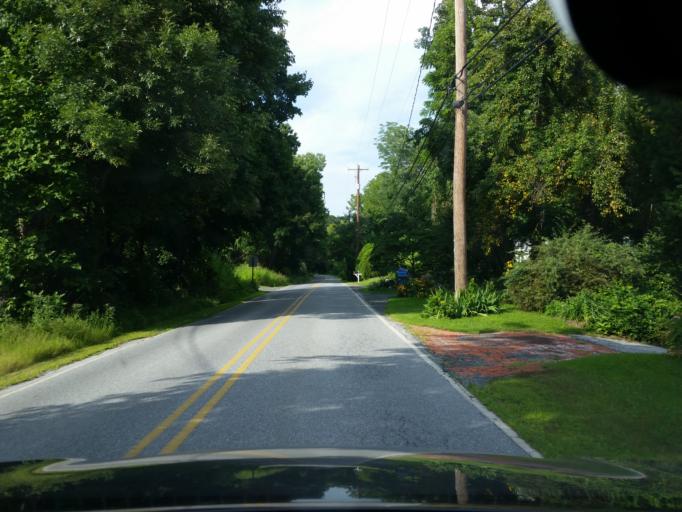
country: US
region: Pennsylvania
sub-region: Perry County
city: Marysville
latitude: 40.3205
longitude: -76.9136
